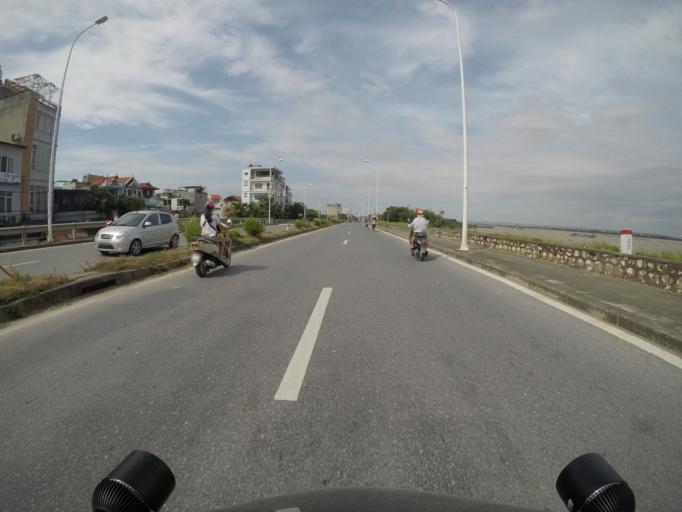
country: VN
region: Ha Noi
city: Tay Ho
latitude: 21.0898
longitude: 105.8040
